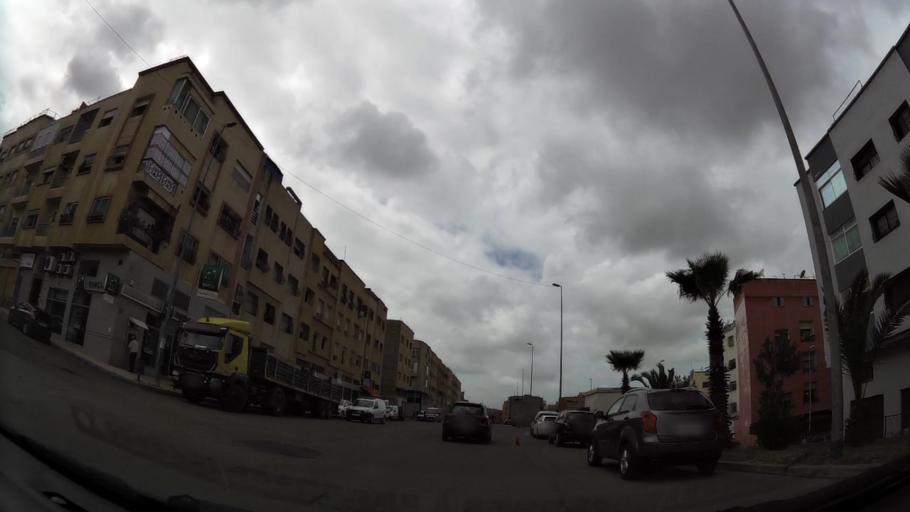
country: MA
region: Grand Casablanca
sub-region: Casablanca
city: Casablanca
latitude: 33.5333
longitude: -7.6048
